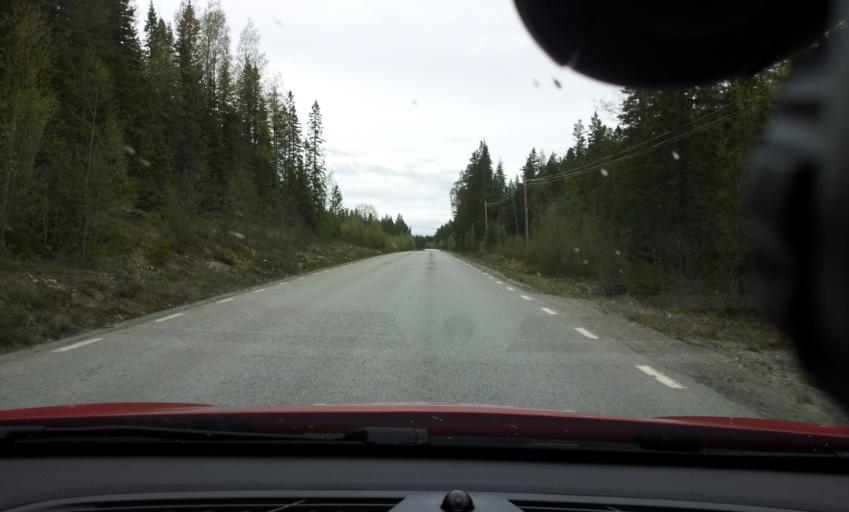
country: SE
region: Jaemtland
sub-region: Bergs Kommun
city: Hoverberg
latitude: 62.7438
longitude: 14.5815
